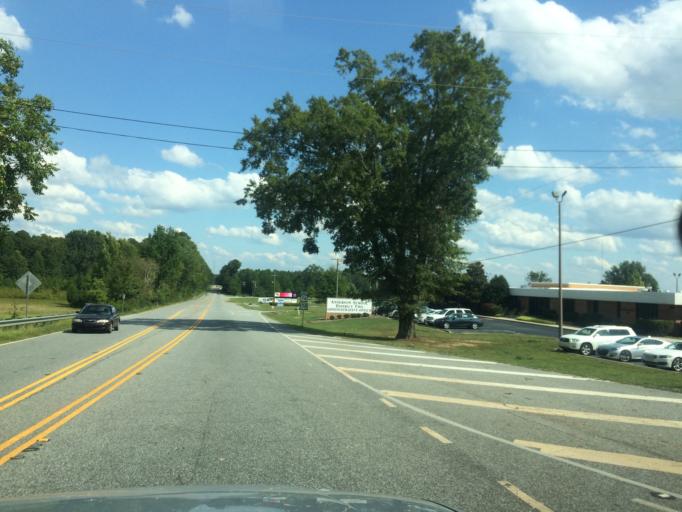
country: US
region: South Carolina
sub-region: Anderson County
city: Honea Path
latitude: 34.4759
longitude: -82.4455
